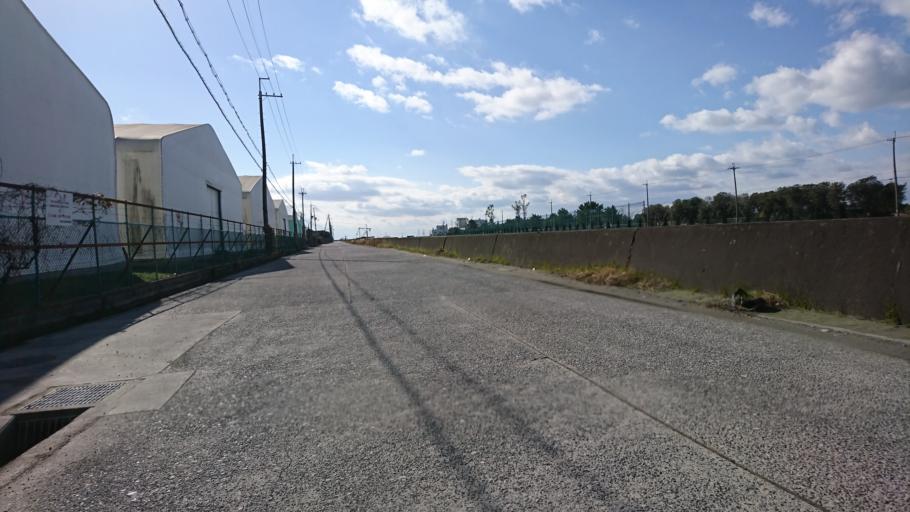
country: JP
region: Hyogo
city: Shirahamacho-usazakiminami
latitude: 34.7686
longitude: 134.7641
